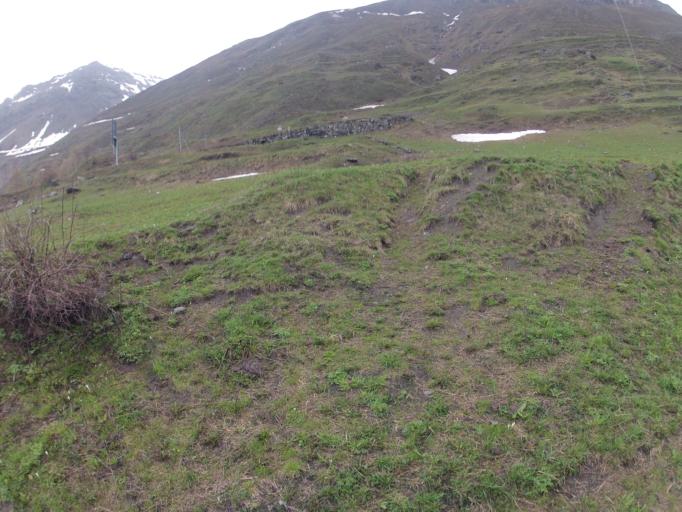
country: IT
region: Piedmont
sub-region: Provincia di Cuneo
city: Crissolo
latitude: 44.7008
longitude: 7.1191
